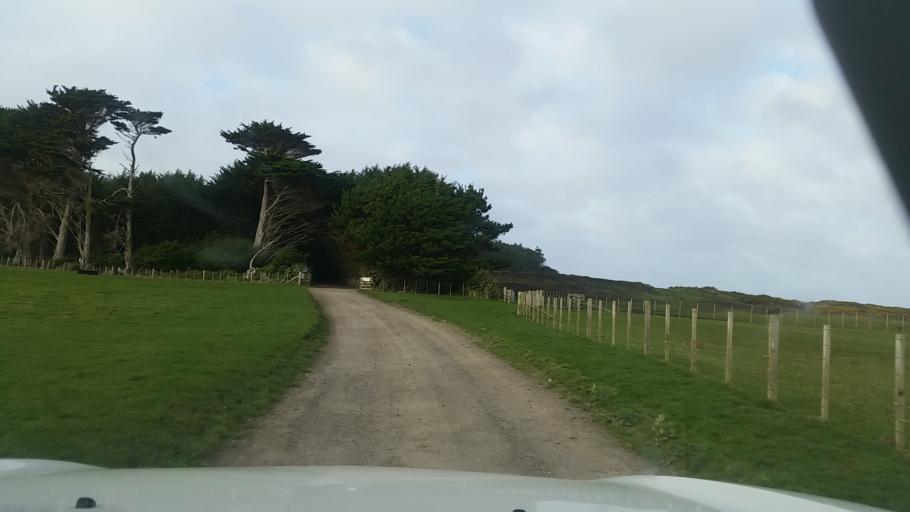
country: NZ
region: Chatham Islands
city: Waitangi
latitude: -43.7380
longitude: -176.2515
